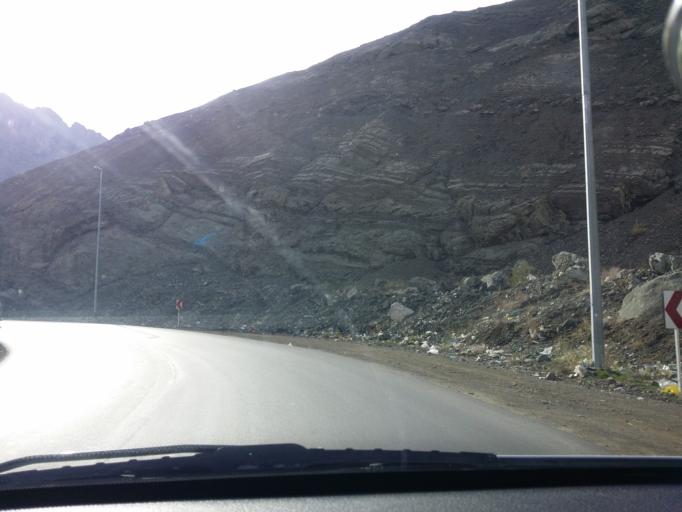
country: IR
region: Alborz
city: Karaj
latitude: 35.9692
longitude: 51.0935
